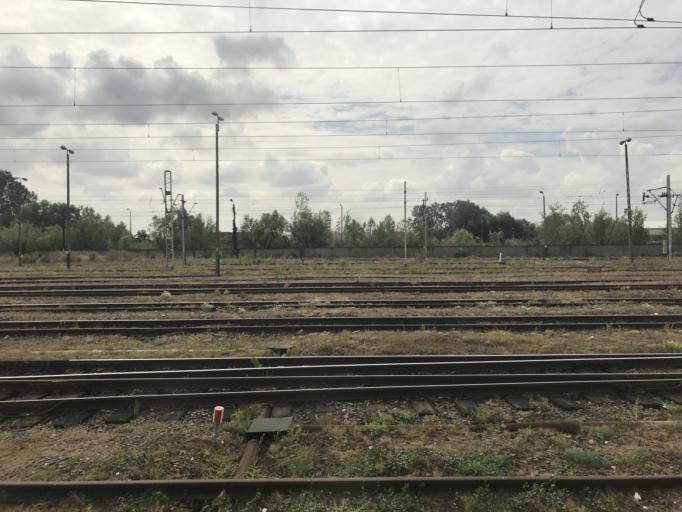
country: PL
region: Greater Poland Voivodeship
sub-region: Powiat gnieznienski
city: Gniezno
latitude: 52.5296
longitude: 17.6062
